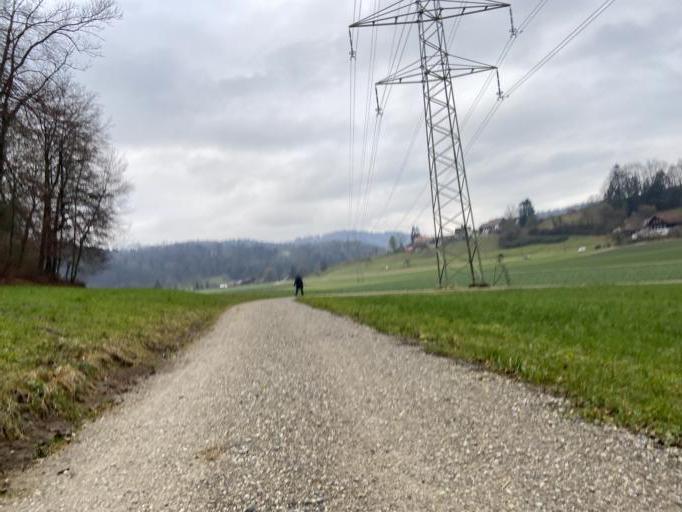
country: CH
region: Zurich
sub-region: Bezirk Winterthur
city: Wuelflingen (Kreis 6) / Niederfeld
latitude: 47.4943
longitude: 8.6823
